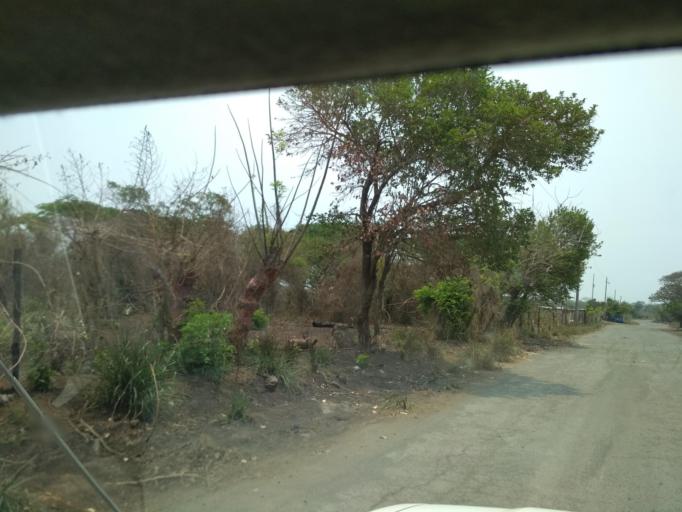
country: MX
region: Veracruz
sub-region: Veracruz
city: Delfino Victoria (Santa Fe)
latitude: 19.2010
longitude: -96.2622
